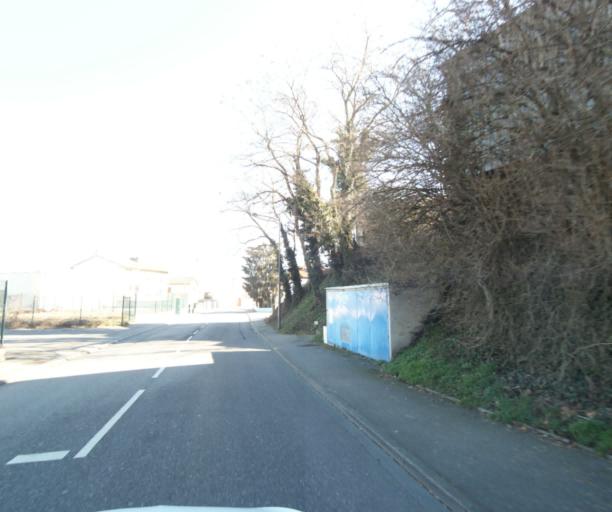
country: FR
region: Lorraine
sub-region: Departement de Meurthe-et-Moselle
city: Maxeville
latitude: 48.7128
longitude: 6.1699
